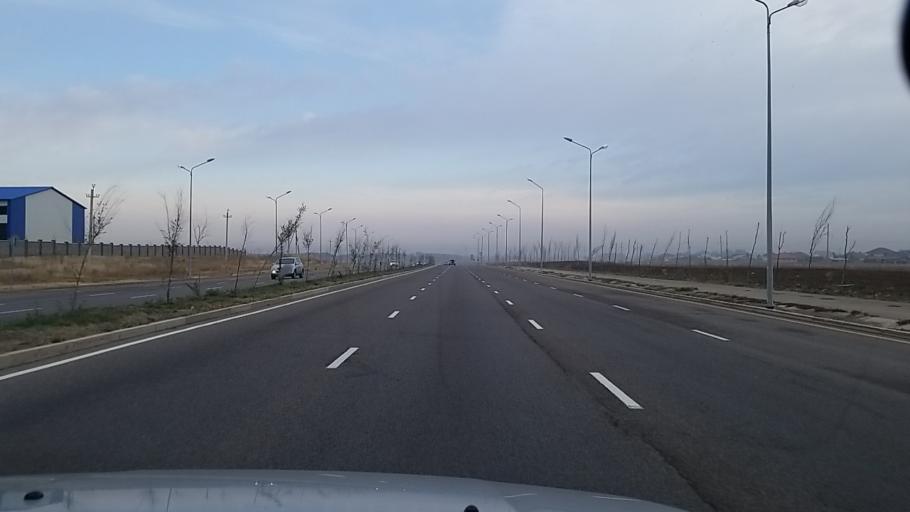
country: KZ
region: Almaty Oblysy
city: Burunday
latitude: 43.3393
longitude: 76.8337
